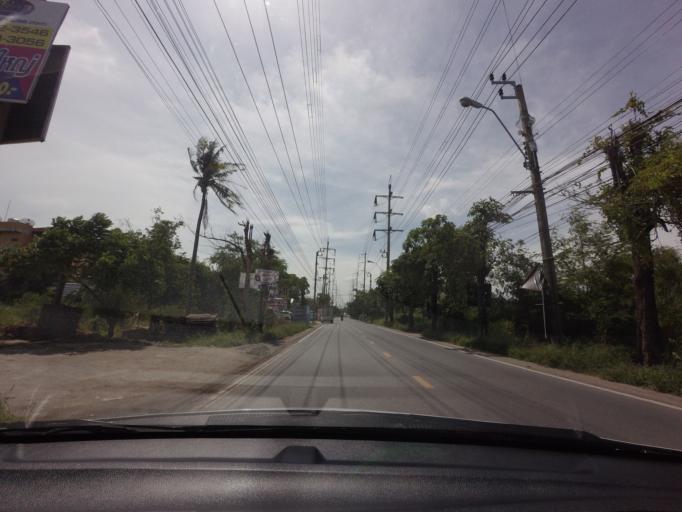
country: TH
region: Bangkok
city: Bang Na
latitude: 13.6197
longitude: 100.6560
